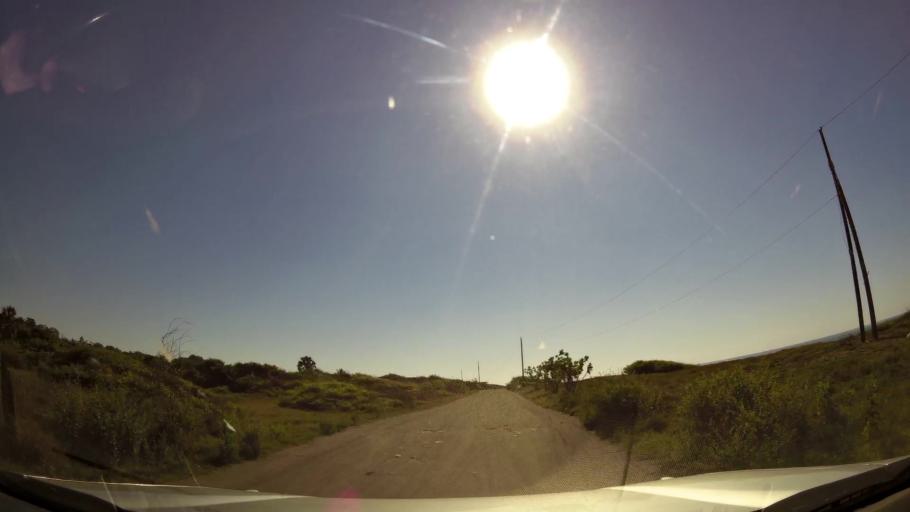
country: GT
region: Jutiapa
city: Pasaco
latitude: 13.8486
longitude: -90.3715
